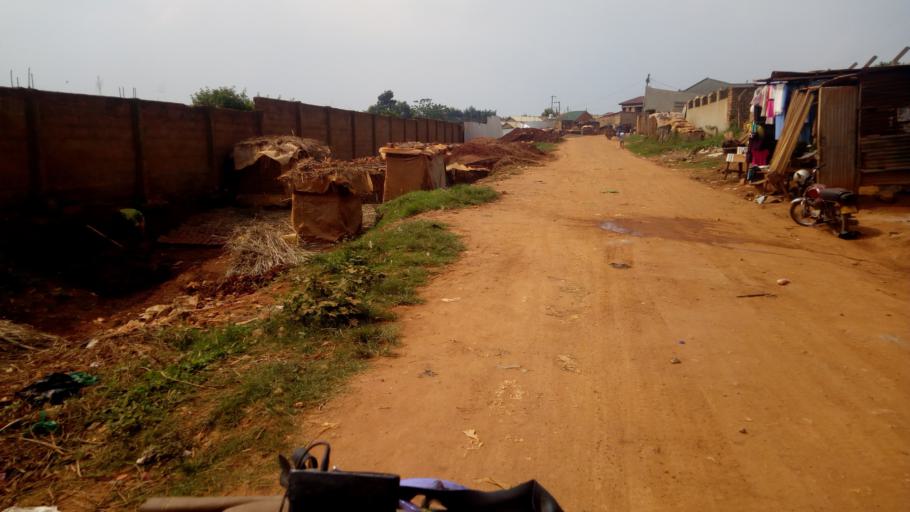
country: UG
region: Central Region
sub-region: Wakiso District
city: Kireka
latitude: 0.3222
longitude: 32.6530
